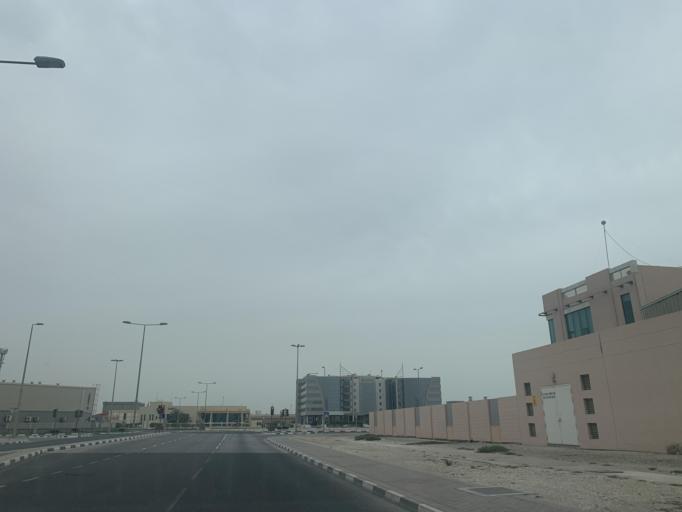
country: BH
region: Muharraq
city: Al Hadd
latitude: 26.2134
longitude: 50.6710
